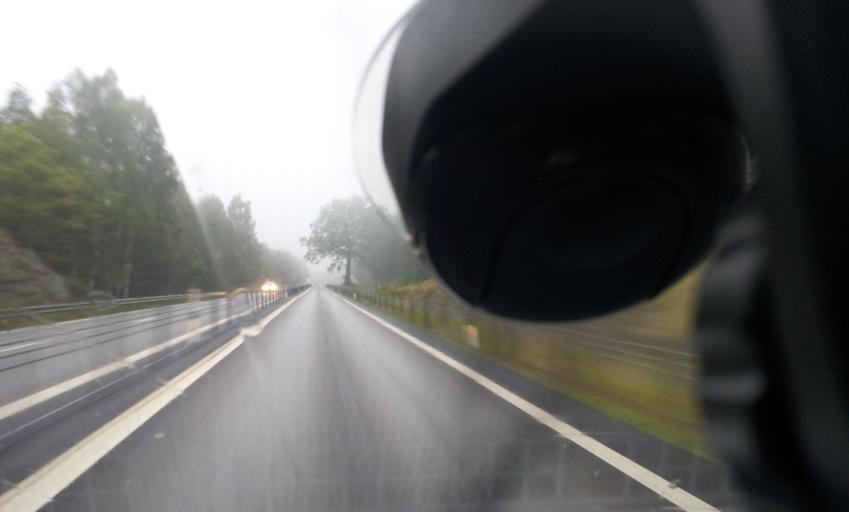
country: SE
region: Kalmar
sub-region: Vasterviks Kommun
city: Vaestervik
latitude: 57.7899
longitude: 16.5247
